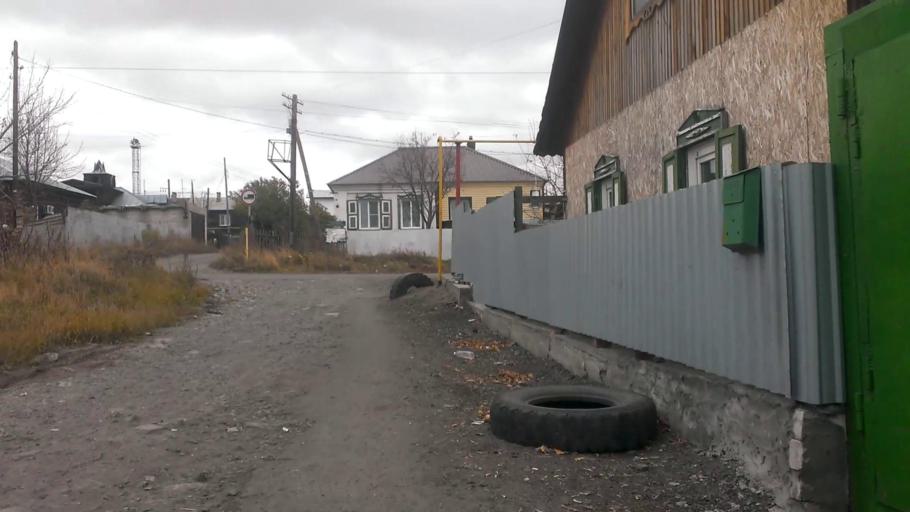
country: RU
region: Altai Krai
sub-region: Gorod Barnaulskiy
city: Barnaul
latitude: 53.3508
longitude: 83.7512
